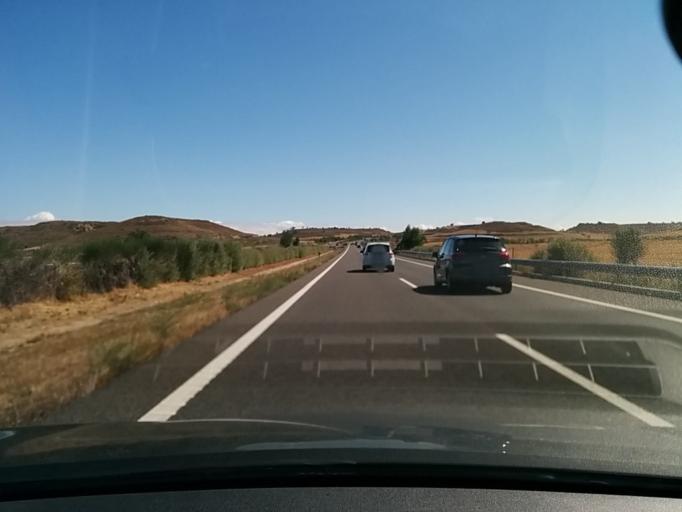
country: ES
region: Aragon
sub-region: Provincia de Huesca
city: Almudebar
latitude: 42.0526
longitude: -0.5489
